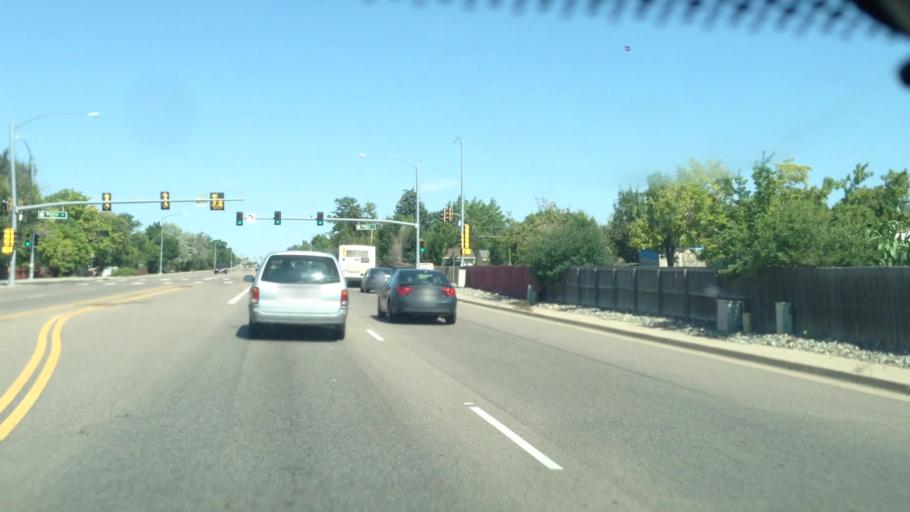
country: US
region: Colorado
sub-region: Adams County
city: Aurora
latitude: 39.7256
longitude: -104.8579
